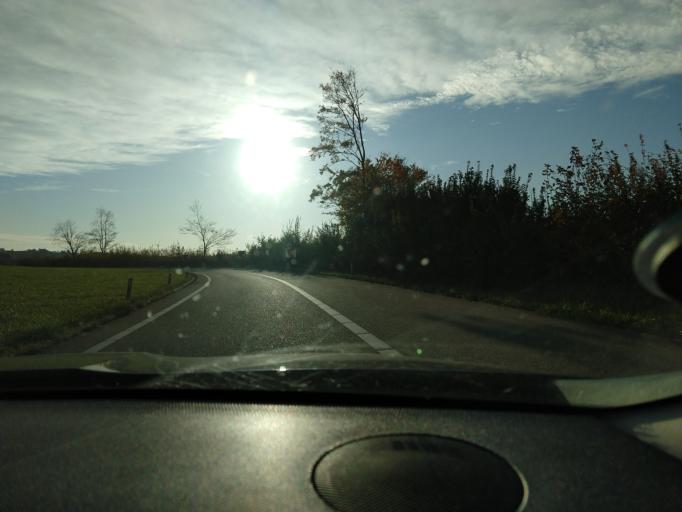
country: NL
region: North Brabant
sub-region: Gemeente Woensdrecht
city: Woensdrecht
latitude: 51.4421
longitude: 4.3080
